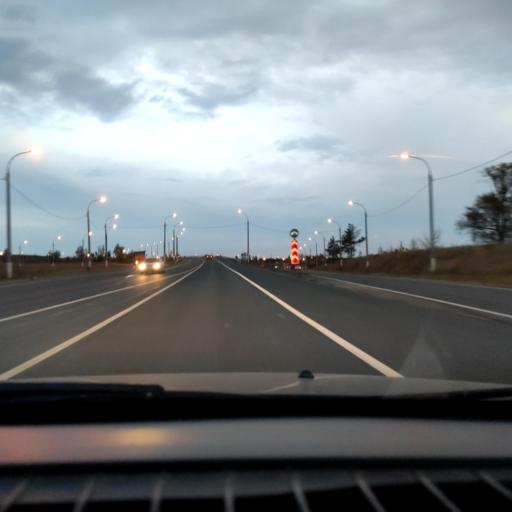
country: RU
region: Samara
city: Zhigulevsk
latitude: 53.5040
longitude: 49.5386
